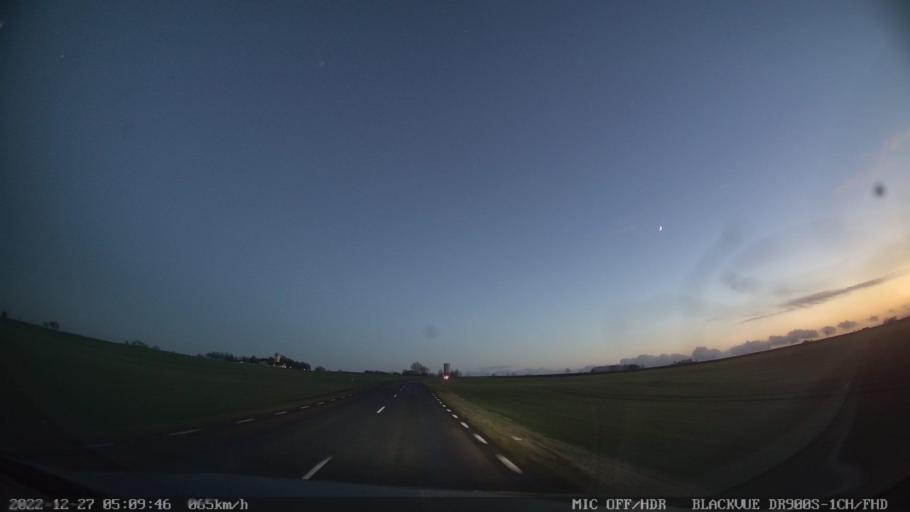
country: SE
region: Skane
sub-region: Simrishamns Kommun
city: Kivik
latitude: 55.5592
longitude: 14.1628
